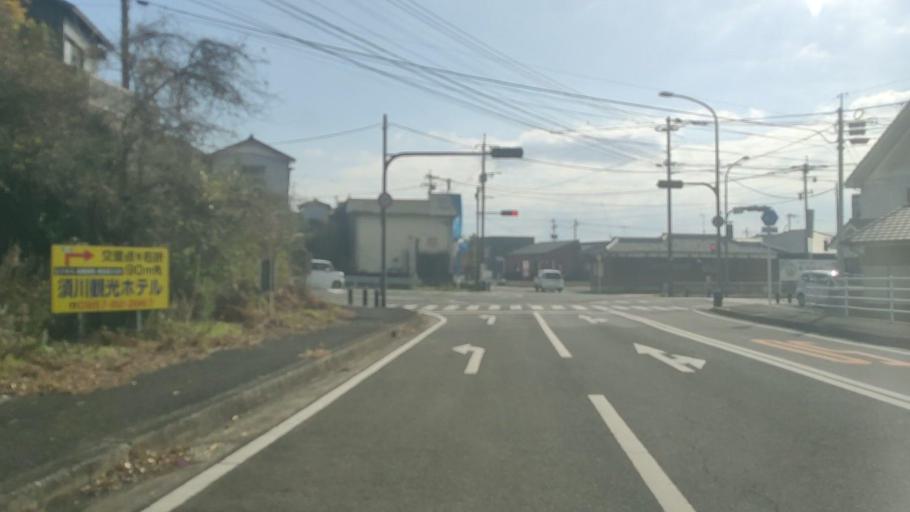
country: JP
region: Nagasaki
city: Shimabara
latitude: 32.6547
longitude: 130.2886
